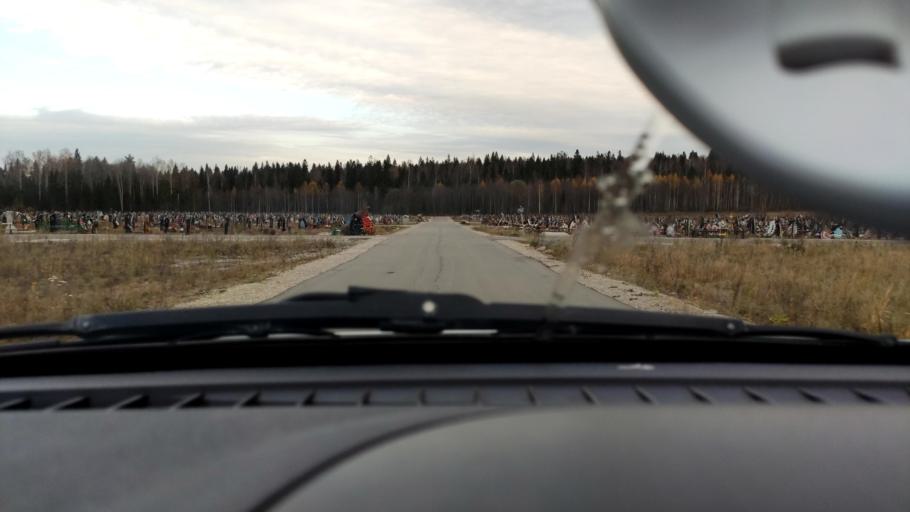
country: RU
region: Perm
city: Kondratovo
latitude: 58.0691
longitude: 56.1359
